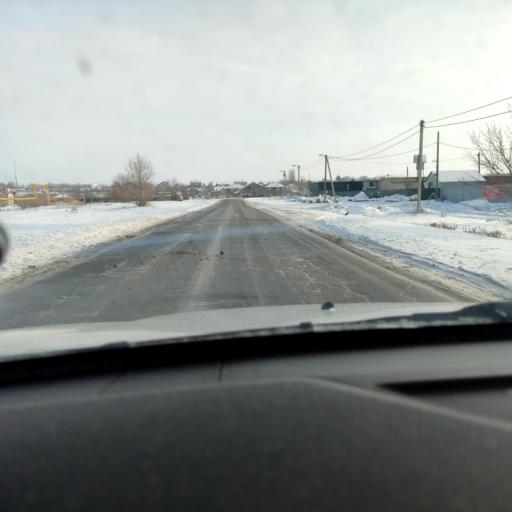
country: RU
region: Samara
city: Smyshlyayevka
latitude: 53.1601
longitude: 50.3832
